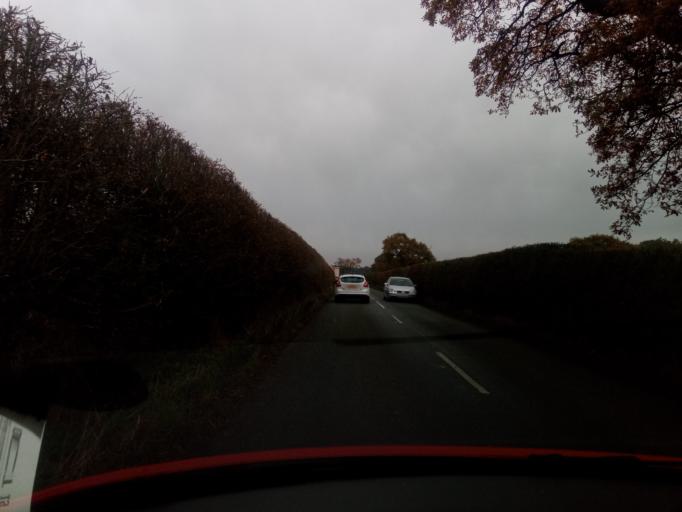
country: GB
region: England
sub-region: Derbyshire
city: Borrowash
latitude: 52.9399
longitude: -1.4060
